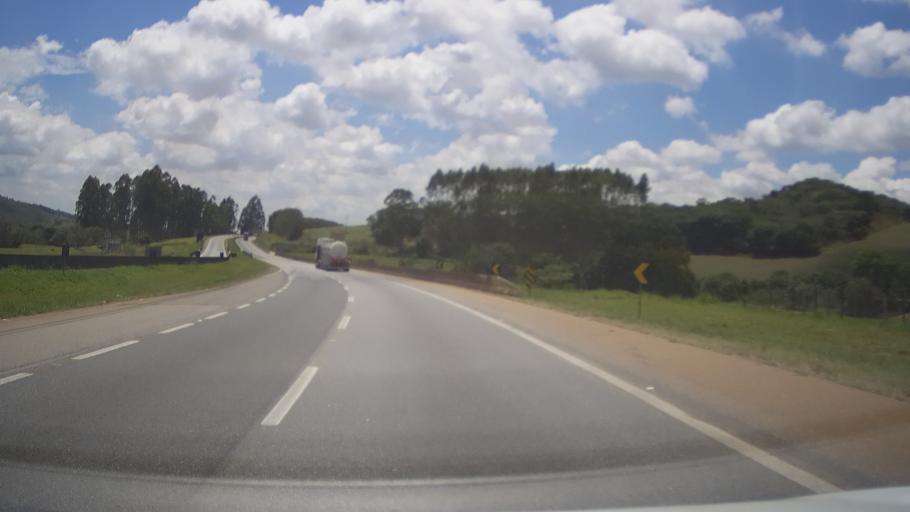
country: BR
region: Minas Gerais
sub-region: Campanha
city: Campanha
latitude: -21.8088
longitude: -45.4824
